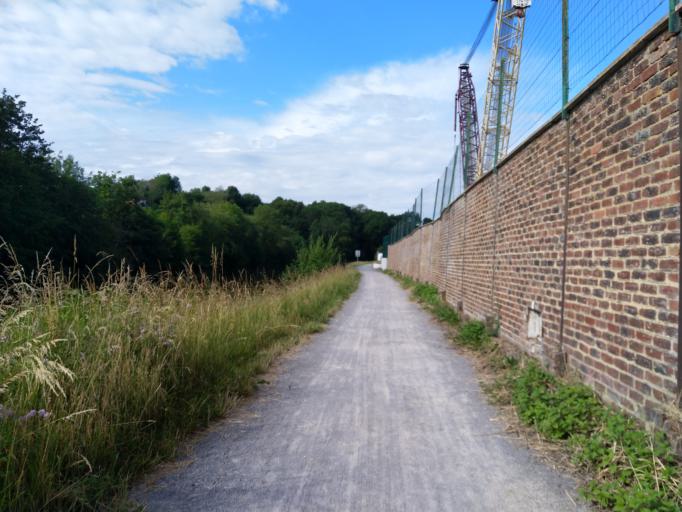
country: BE
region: Wallonia
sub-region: Province du Hainaut
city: Erquelinnes
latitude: 50.3002
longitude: 4.1088
